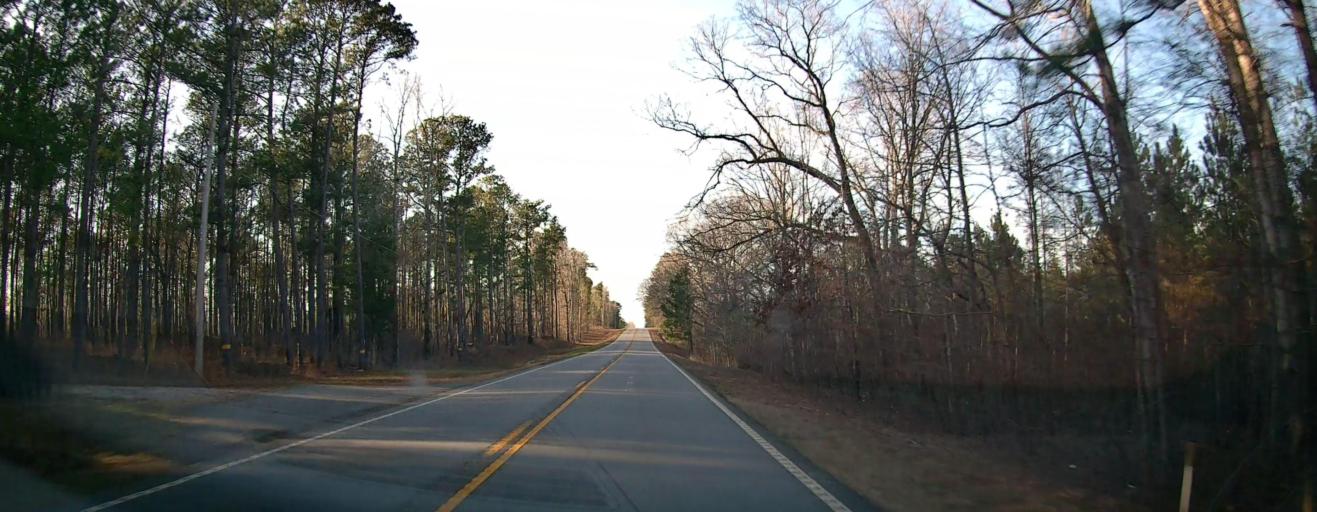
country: US
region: Alabama
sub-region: Chambers County
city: Valley
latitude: 32.7811
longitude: -85.0924
